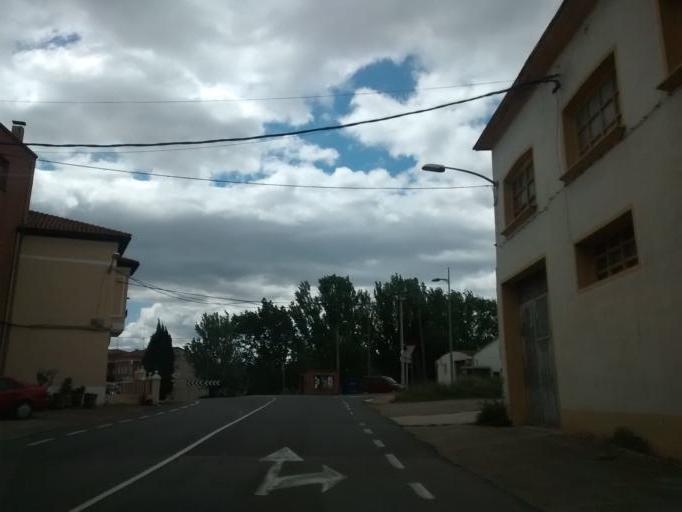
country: ES
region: La Rioja
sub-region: Provincia de La Rioja
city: Pradejon
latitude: 42.3198
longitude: -2.0922
